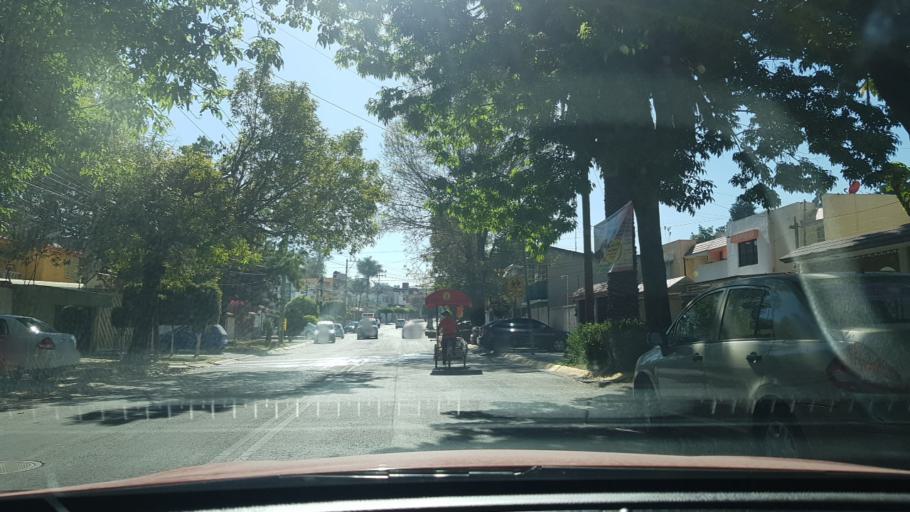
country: MX
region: Mexico
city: Cuautitlan Izcalli
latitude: 19.6477
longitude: -99.2011
